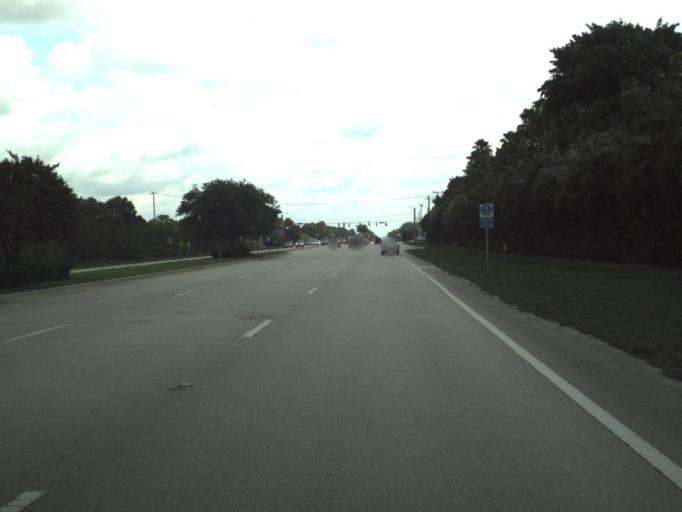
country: US
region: Florida
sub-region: Palm Beach County
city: Juno Beach
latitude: 26.8799
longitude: -80.0952
